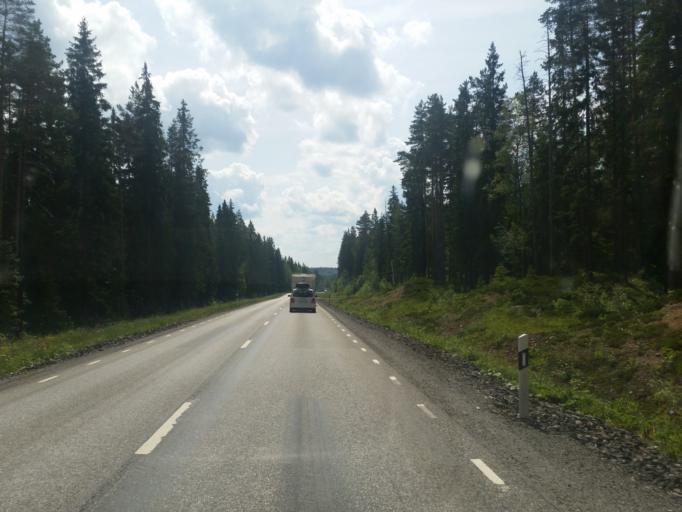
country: SE
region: OErebro
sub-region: Ljusnarsbergs Kommun
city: Kopparberg
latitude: 59.9180
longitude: 15.0217
